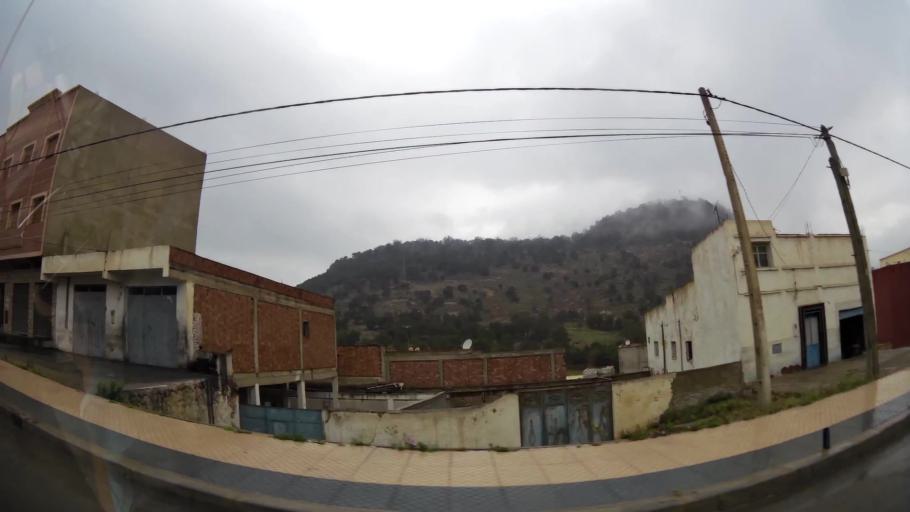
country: MA
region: Oriental
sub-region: Nador
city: Nador
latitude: 35.1509
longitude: -3.0134
